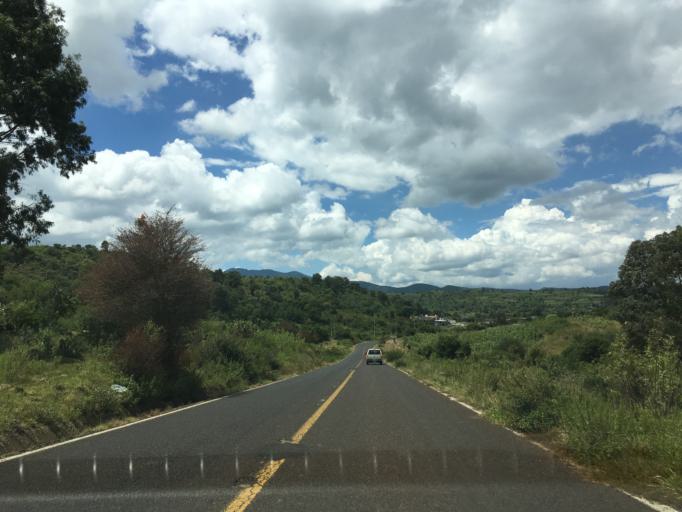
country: MX
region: Michoacan
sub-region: Morelia
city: Cuto de la Esperanza
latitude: 19.7779
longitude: -101.4260
